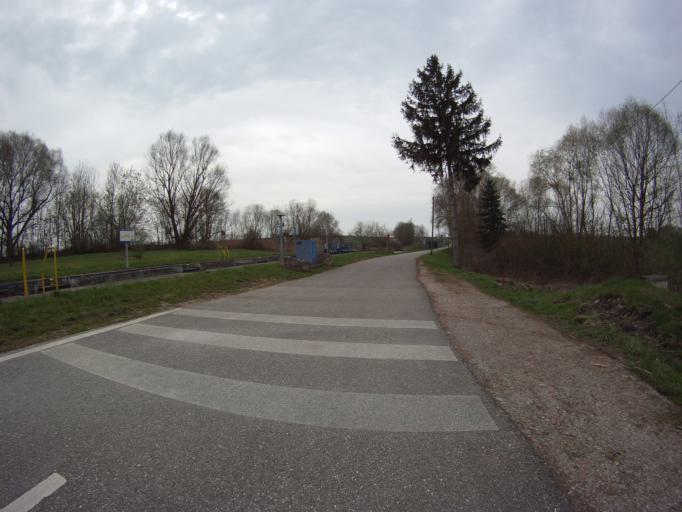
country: FR
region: Lorraine
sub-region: Departement de Meurthe-et-Moselle
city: Fleville-devant-Nancy
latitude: 48.6261
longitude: 6.2183
